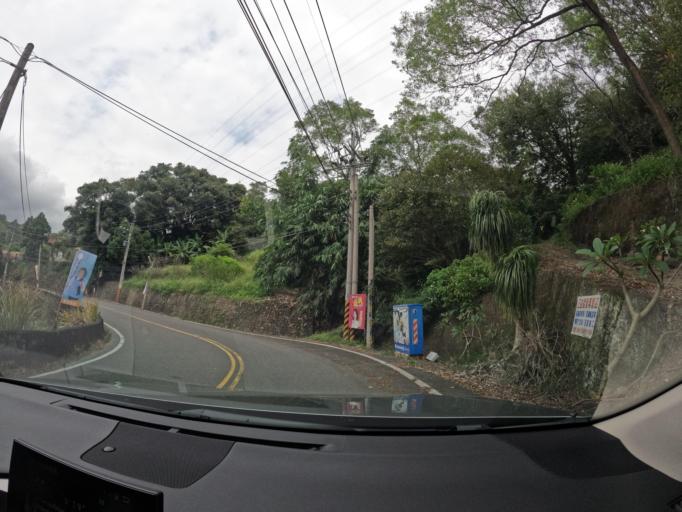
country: TW
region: Taiwan
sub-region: Miaoli
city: Miaoli
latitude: 24.3772
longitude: 120.8656
